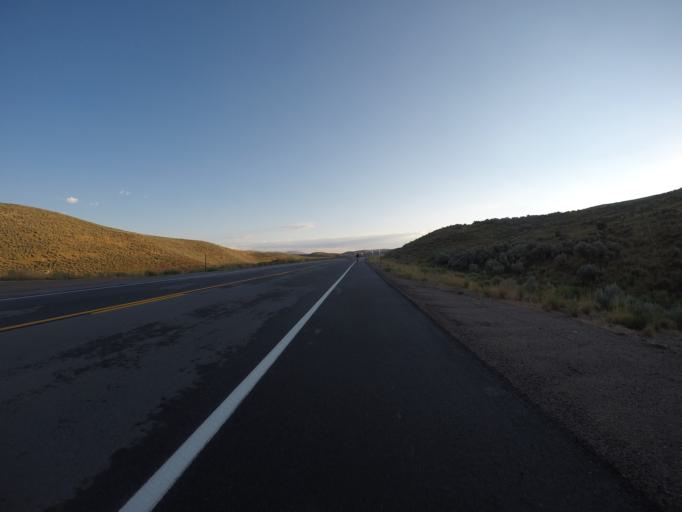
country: US
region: Wyoming
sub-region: Lincoln County
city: Kemmerer
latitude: 41.8547
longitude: -110.5291
